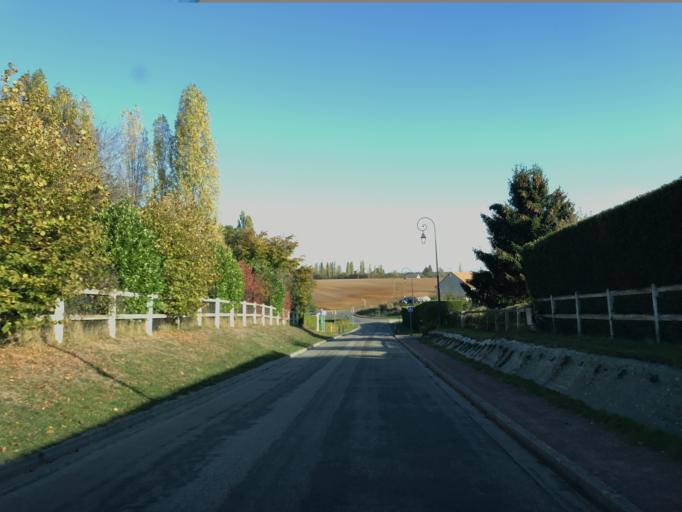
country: FR
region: Haute-Normandie
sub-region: Departement de l'Eure
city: Gravigny
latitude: 49.0765
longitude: 1.2546
